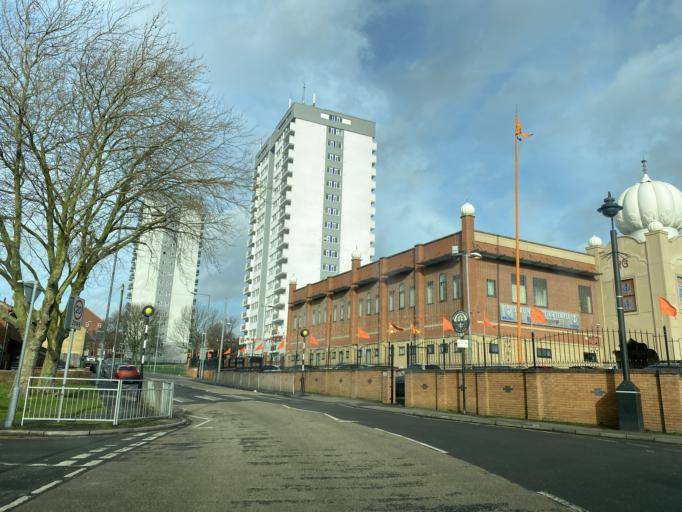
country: GB
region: England
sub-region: Walsall
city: Walsall
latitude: 52.5736
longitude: -1.9790
